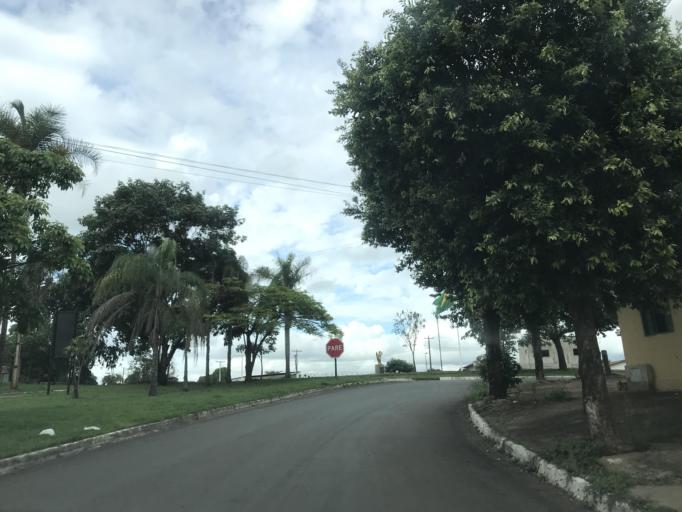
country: BR
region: Goias
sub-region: Bela Vista De Goias
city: Bela Vista de Goias
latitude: -17.0514
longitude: -48.6658
